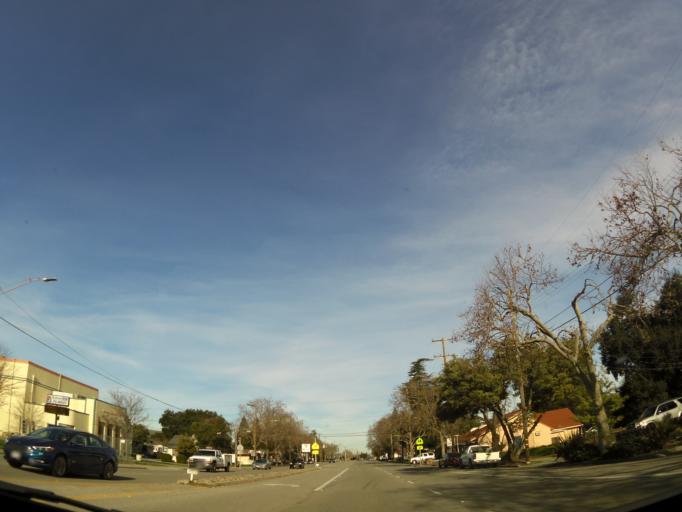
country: US
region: California
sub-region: Santa Clara County
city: Morgan Hill
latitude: 37.1320
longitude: -121.6559
